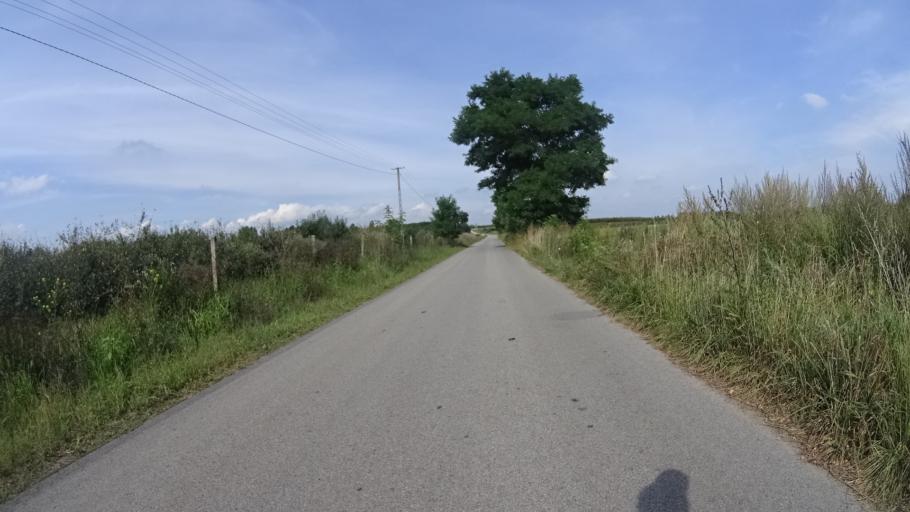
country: PL
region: Masovian Voivodeship
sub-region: Powiat grojecki
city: Goszczyn
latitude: 51.6821
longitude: 20.8401
